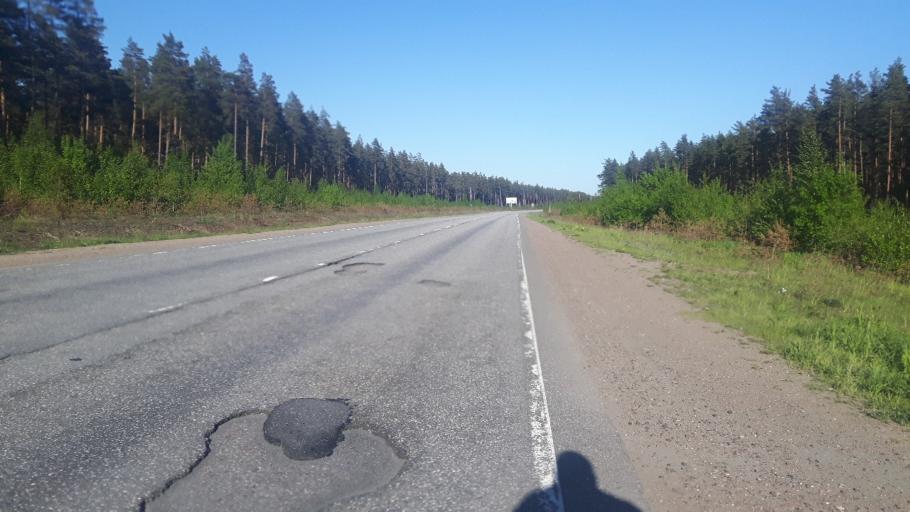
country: RU
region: Leningrad
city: Lebyazh'ye
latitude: 60.1680
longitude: 29.2312
